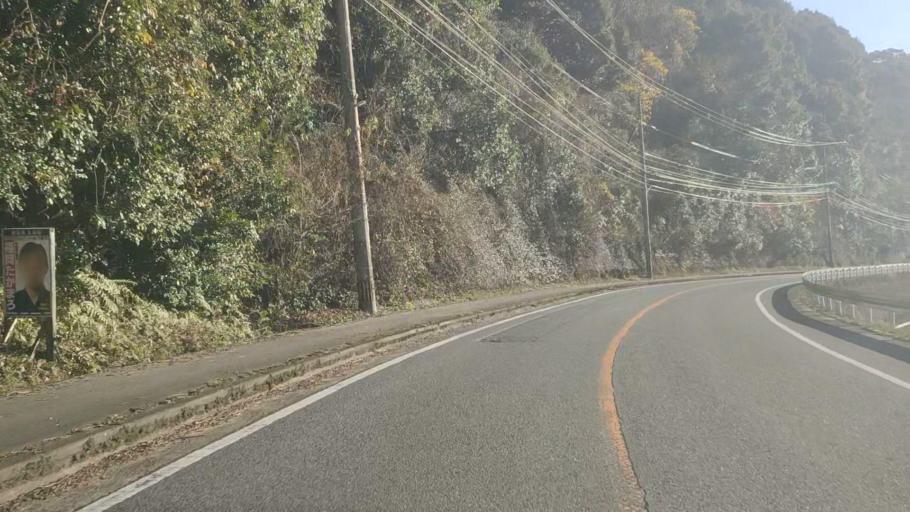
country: JP
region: Saga Prefecture
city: Saga-shi
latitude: 33.3487
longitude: 130.2496
